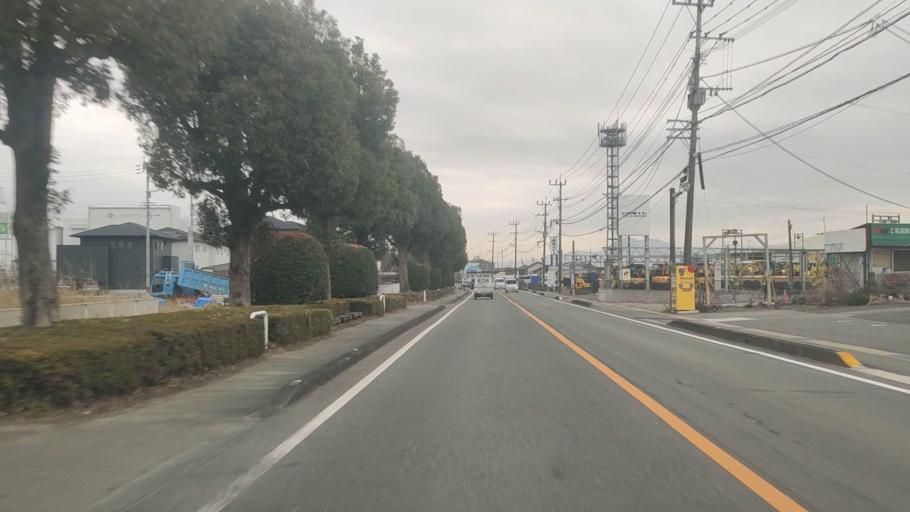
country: JP
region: Kumamoto
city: Ozu
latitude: 32.8270
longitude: 130.7995
